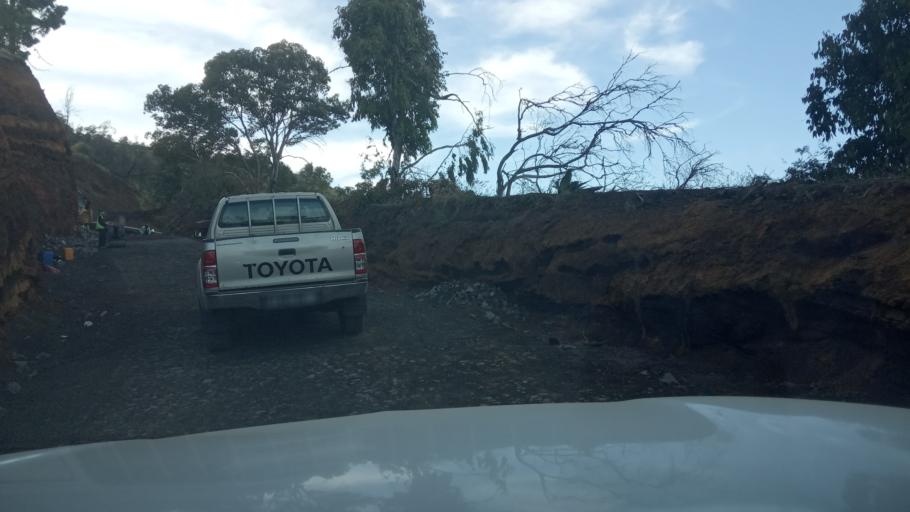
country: CV
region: Mosteiros
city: Porto dos Mosteiros
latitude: 14.9996
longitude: -24.3456
